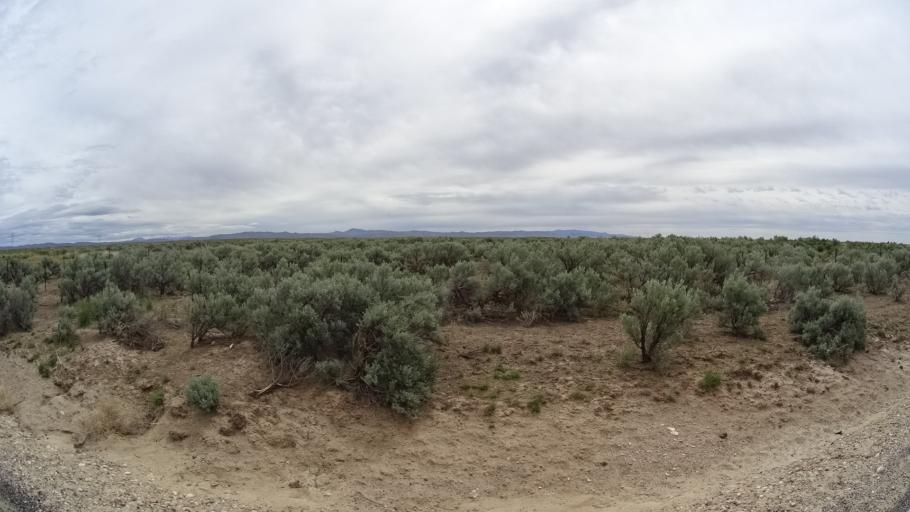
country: US
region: Idaho
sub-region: Ada County
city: Boise
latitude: 43.3611
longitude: -116.0049
